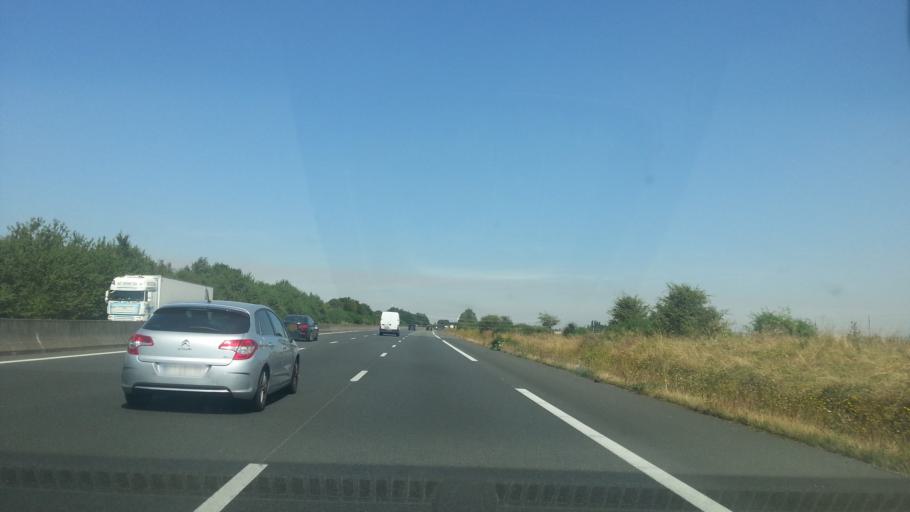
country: FR
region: Centre
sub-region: Departement d'Eure-et-Loir
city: Janville
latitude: 48.2155
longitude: 1.8471
